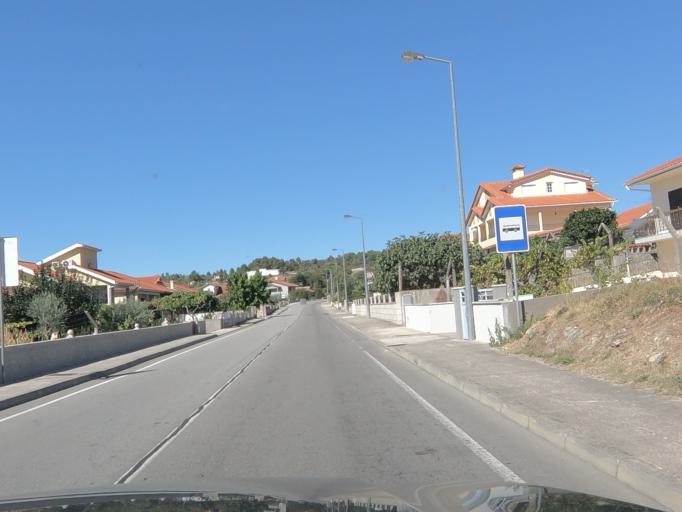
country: PT
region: Vila Real
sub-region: Valpacos
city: Valpacos
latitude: 41.6251
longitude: -7.3124
